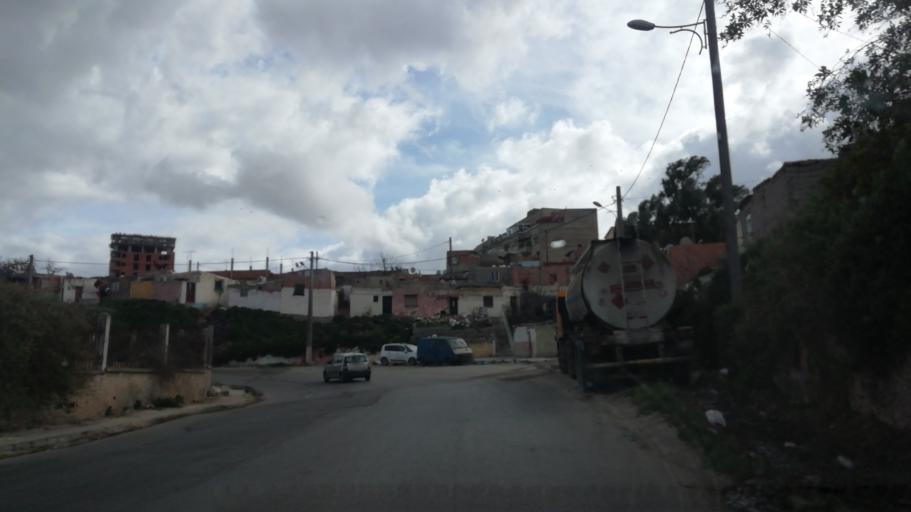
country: DZ
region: Oran
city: Oran
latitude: 35.6930
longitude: -0.6585
